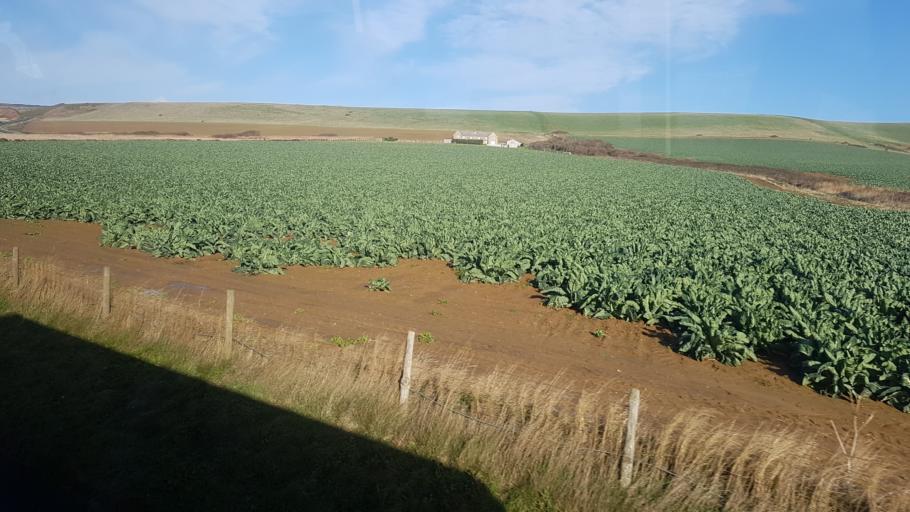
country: GB
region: England
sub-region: Isle of Wight
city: Freshwater
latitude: 50.6557
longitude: -1.4670
